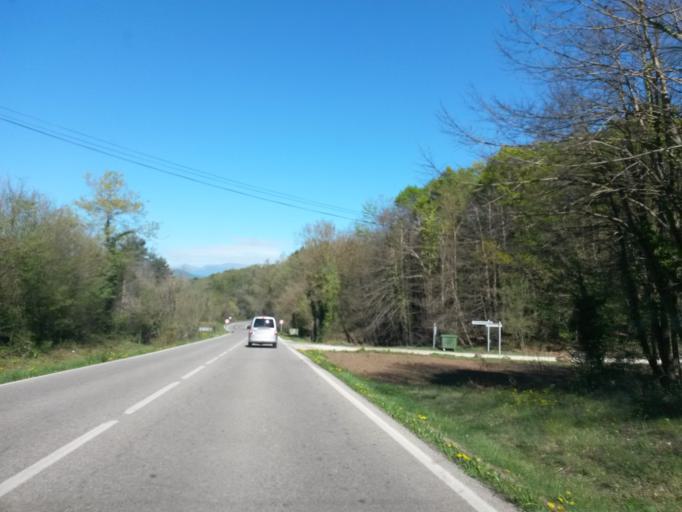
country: ES
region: Catalonia
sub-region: Provincia de Girona
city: Sant Cristofol de les Fonts
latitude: 42.1508
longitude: 2.5273
